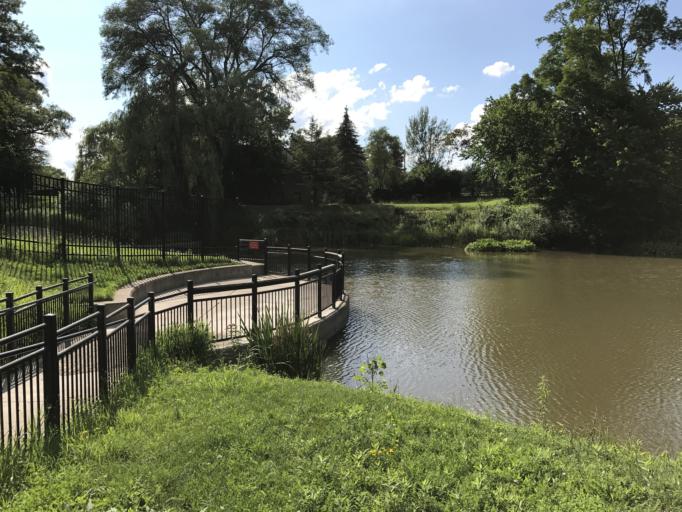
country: US
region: Michigan
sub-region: Oakland County
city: Franklin
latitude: 42.4645
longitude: -83.3161
